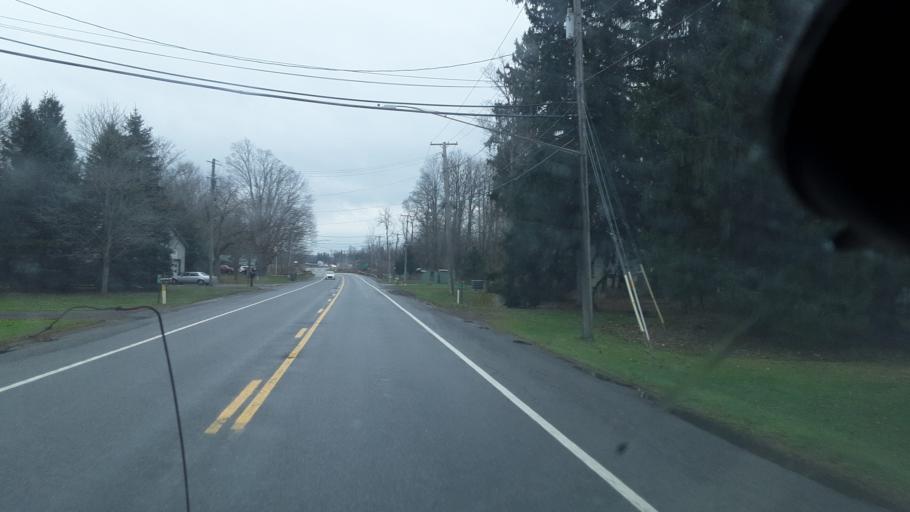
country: US
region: New York
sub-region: Erie County
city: Holland
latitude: 42.6899
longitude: -78.5696
